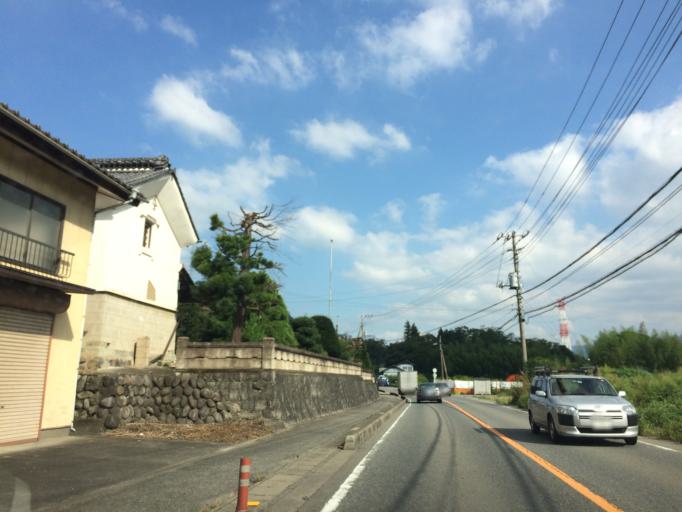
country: JP
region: Gunma
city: Nakanojomachi
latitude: 36.5672
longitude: 138.7483
